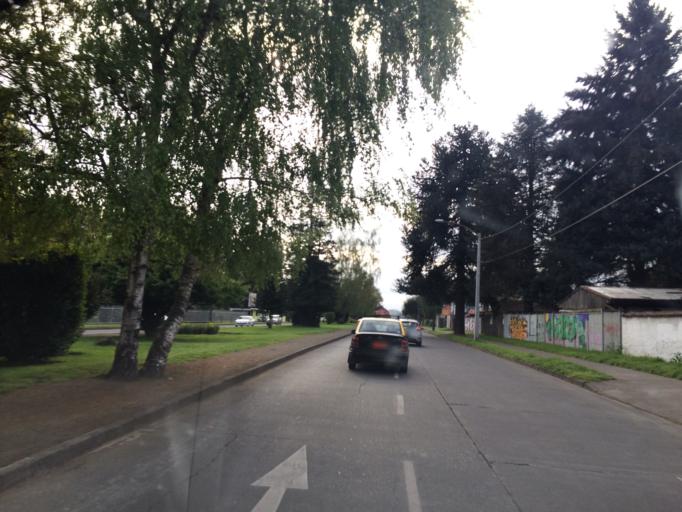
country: CL
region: Araucania
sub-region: Provincia de Cautin
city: Temuco
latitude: -38.7408
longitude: -72.6189
